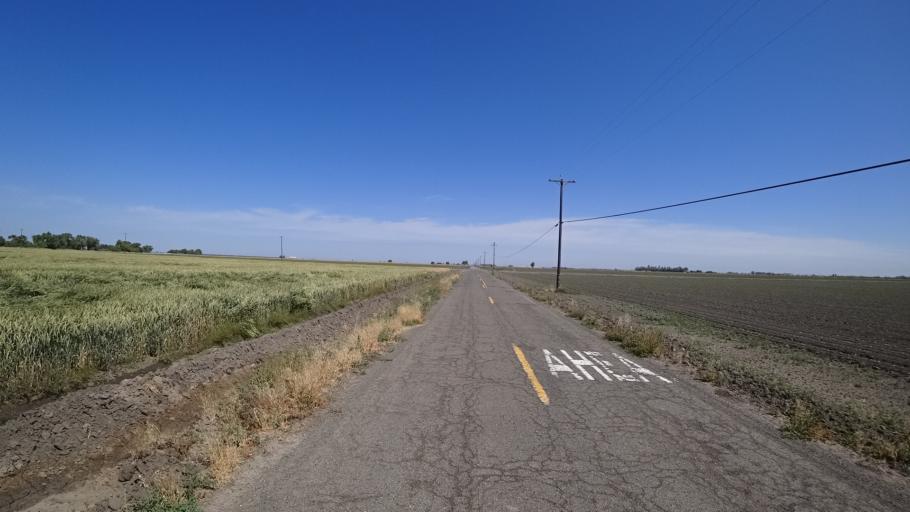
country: US
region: California
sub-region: Kings County
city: Stratford
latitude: 36.1956
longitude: -119.8162
